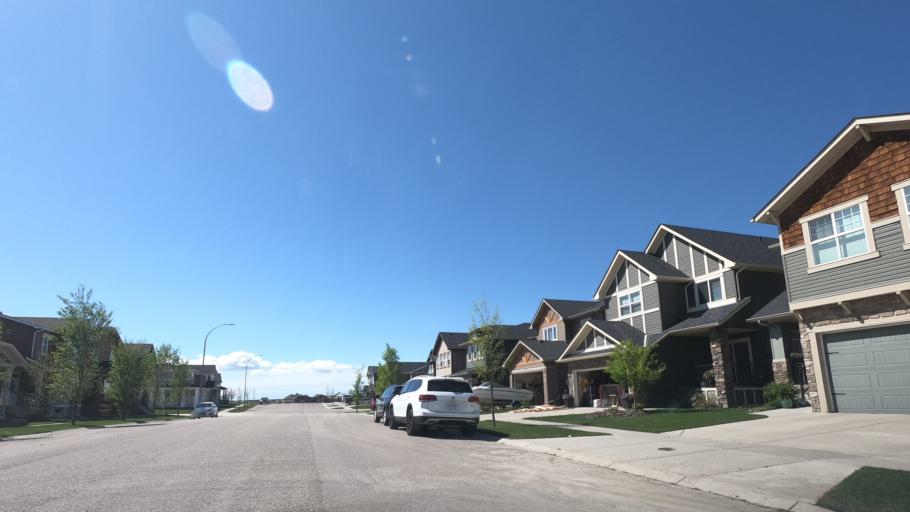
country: CA
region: Alberta
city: Airdrie
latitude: 51.2646
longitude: -113.9749
